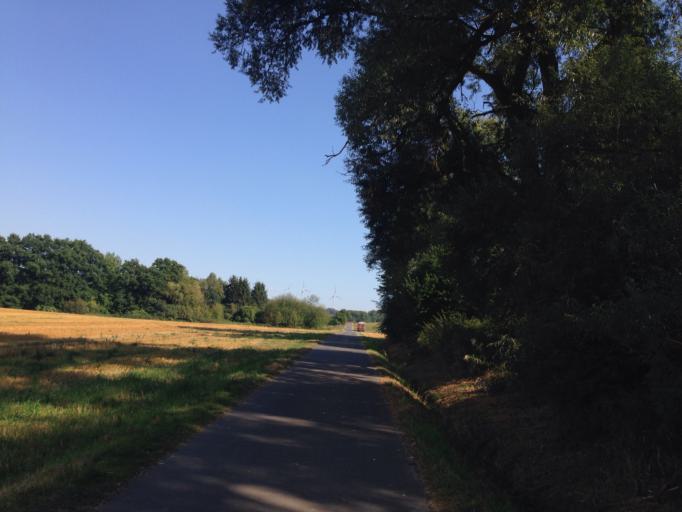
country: DE
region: Hesse
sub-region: Regierungsbezirk Giessen
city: Rabenau
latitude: 50.6700
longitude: 8.8639
